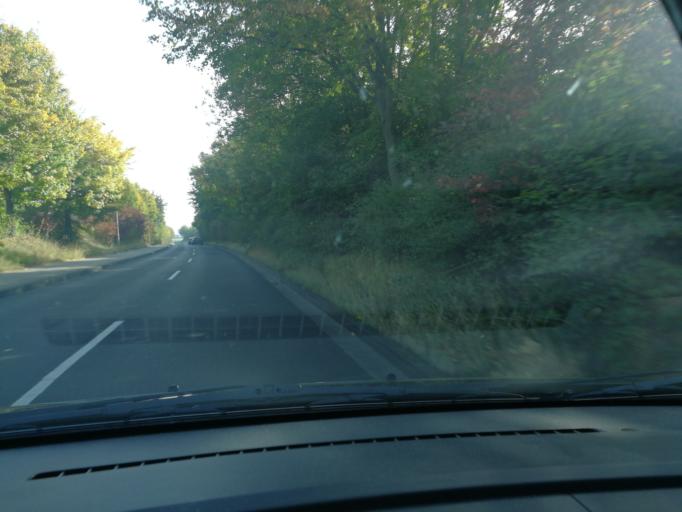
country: DE
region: Hesse
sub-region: Regierungsbezirk Darmstadt
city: Friedberg
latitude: 50.3198
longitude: 8.7607
